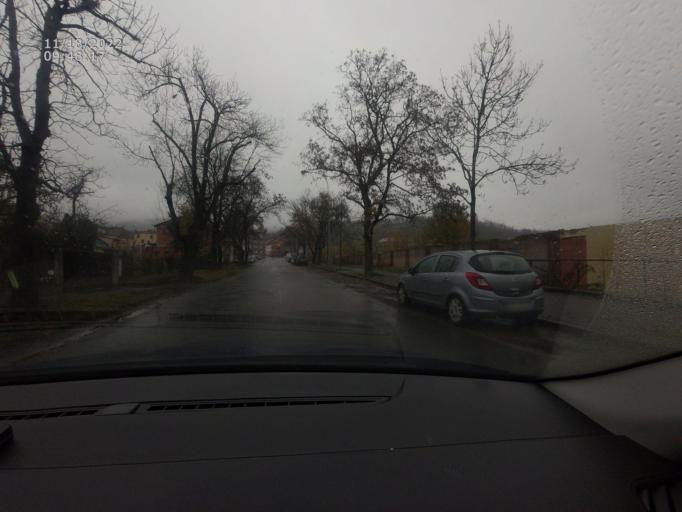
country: CZ
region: Central Bohemia
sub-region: Okres Beroun
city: Beroun
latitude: 49.9584
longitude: 14.0647
